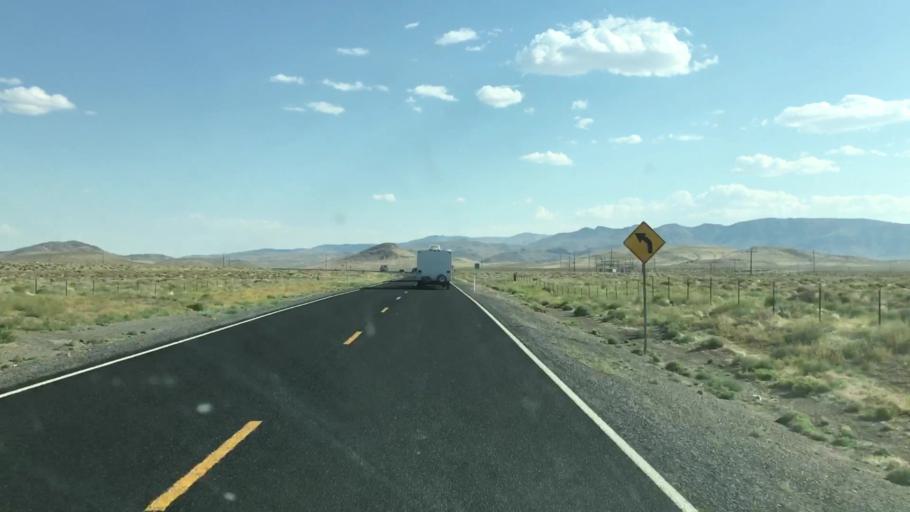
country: US
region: Nevada
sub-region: Lyon County
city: Fernley
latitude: 39.6577
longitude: -119.3297
